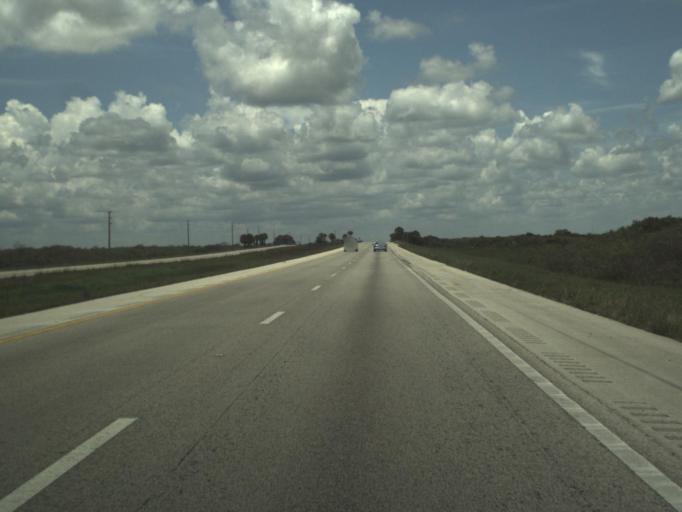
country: US
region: Florida
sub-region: Broward County
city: Weston
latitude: 26.1558
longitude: -80.7590
